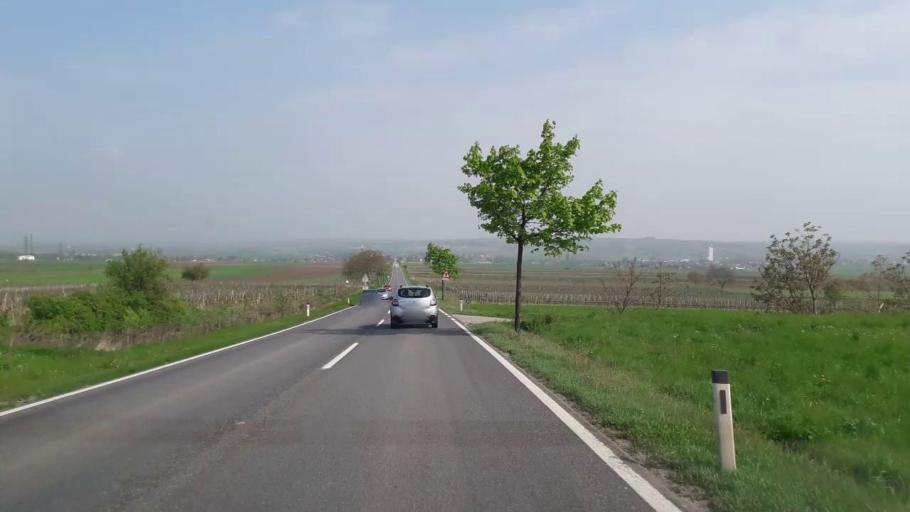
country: AT
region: Lower Austria
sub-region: Politischer Bezirk Hollabrunn
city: Haugsdorf
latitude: 48.6867
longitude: 16.0588
